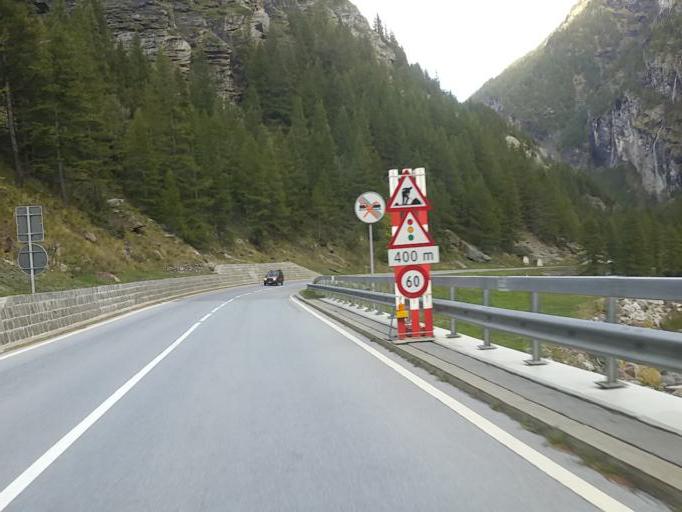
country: IT
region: Piedmont
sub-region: Provincia Verbano-Cusio-Ossola
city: Antronapiana
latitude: 46.1857
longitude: 8.0784
